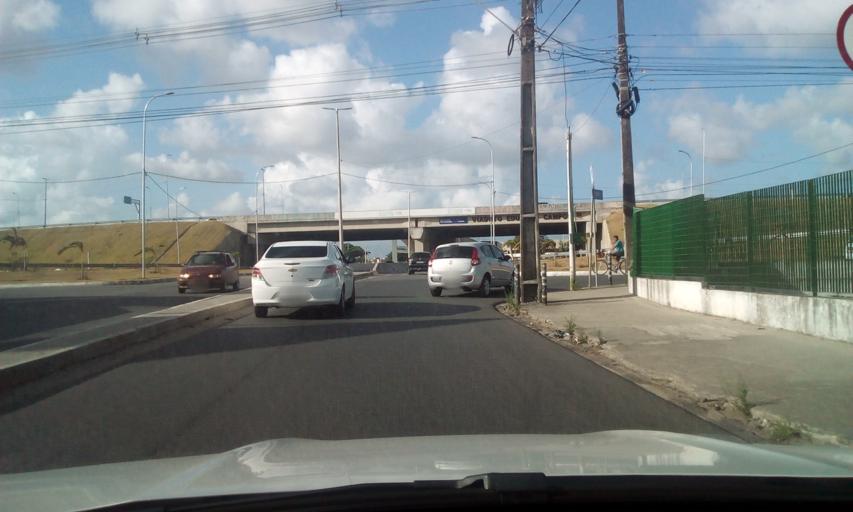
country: BR
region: Paraiba
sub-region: Joao Pessoa
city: Joao Pessoa
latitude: -7.1705
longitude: -34.8742
